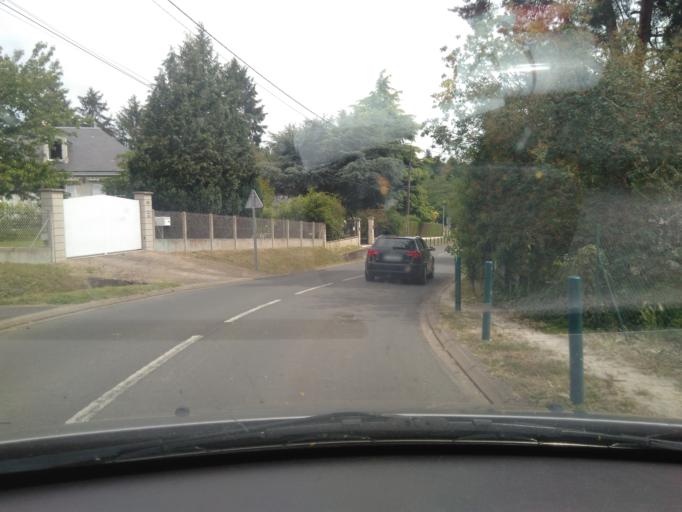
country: FR
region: Centre
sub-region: Departement d'Indre-et-Loire
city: Amboise
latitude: 47.4044
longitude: 1.0014
